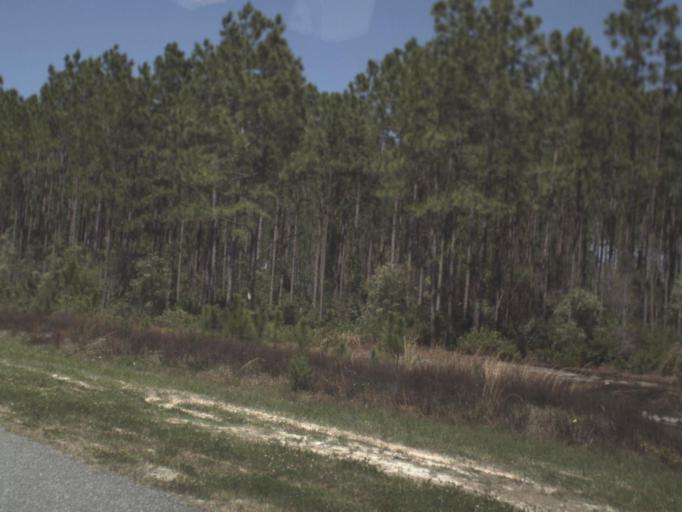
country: US
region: Florida
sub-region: Gulf County
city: Port Saint Joe
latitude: 29.8869
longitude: -85.3465
